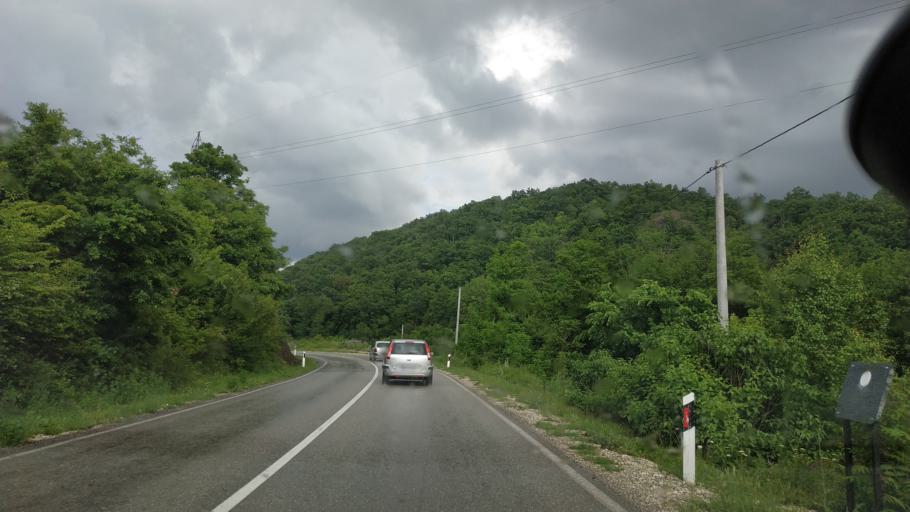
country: RS
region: Central Serbia
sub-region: Borski Okrug
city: Bor
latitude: 44.0561
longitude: 22.0574
